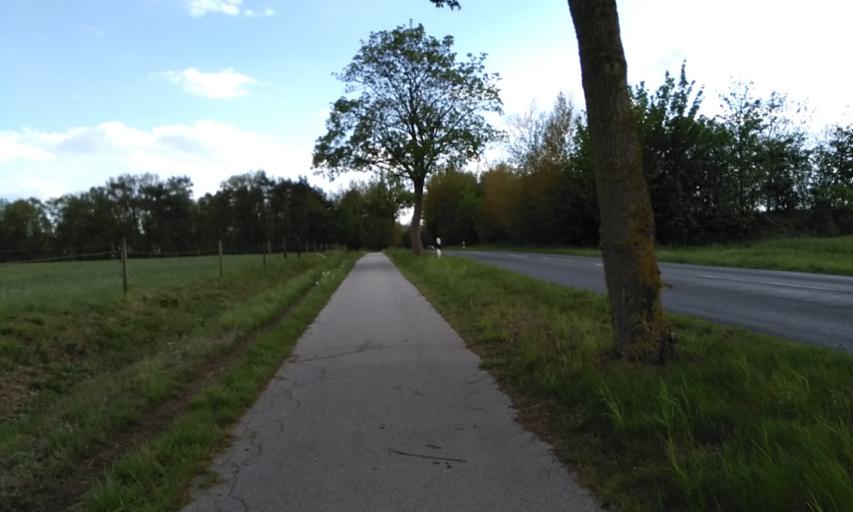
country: DE
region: Lower Saxony
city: Buxtehude
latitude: 53.4424
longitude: 9.6651
